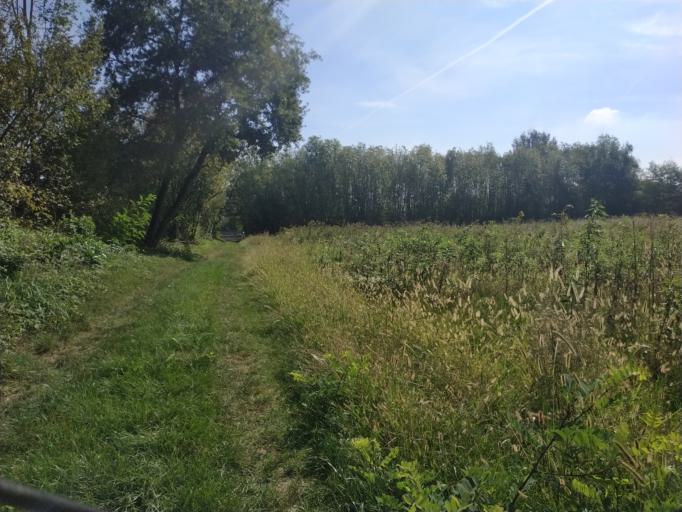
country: IT
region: Piedmont
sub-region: Provincia di Torino
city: Orio Canavese
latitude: 45.3159
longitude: 7.8502
